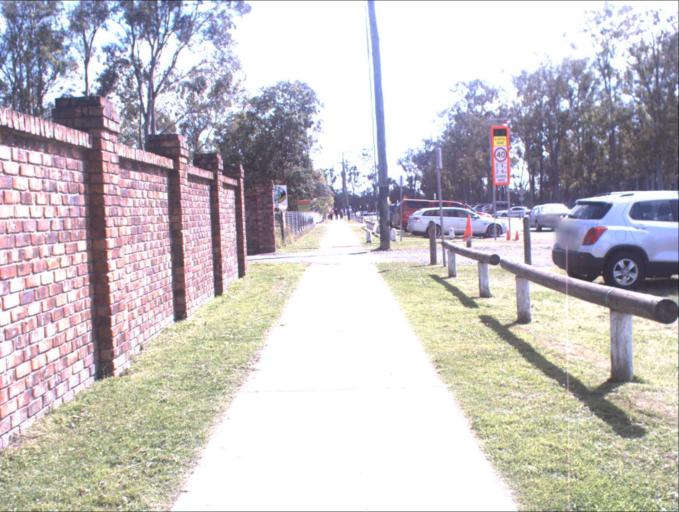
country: AU
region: Queensland
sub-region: Logan
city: Park Ridge South
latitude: -27.7126
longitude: 152.9773
